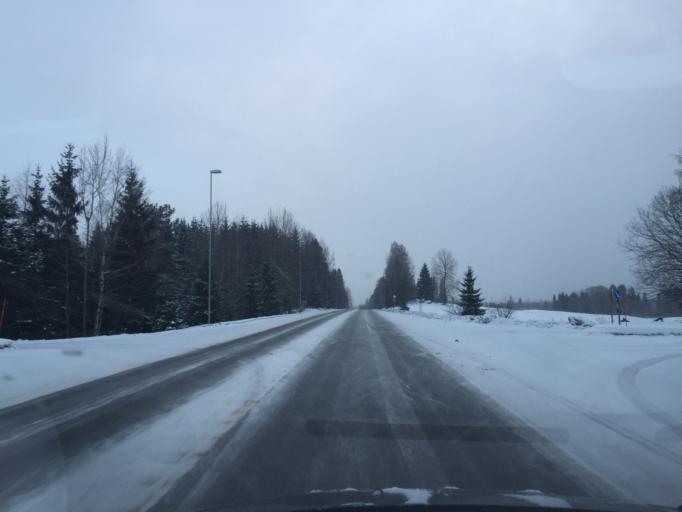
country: NO
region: Hedmark
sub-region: Elverum
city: Elverum
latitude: 60.9194
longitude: 11.6554
